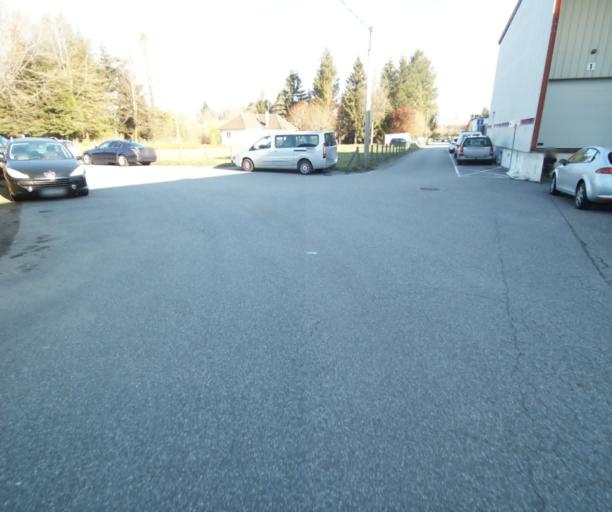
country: FR
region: Limousin
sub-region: Departement de la Correze
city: Correze
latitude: 45.3314
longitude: 1.8875
